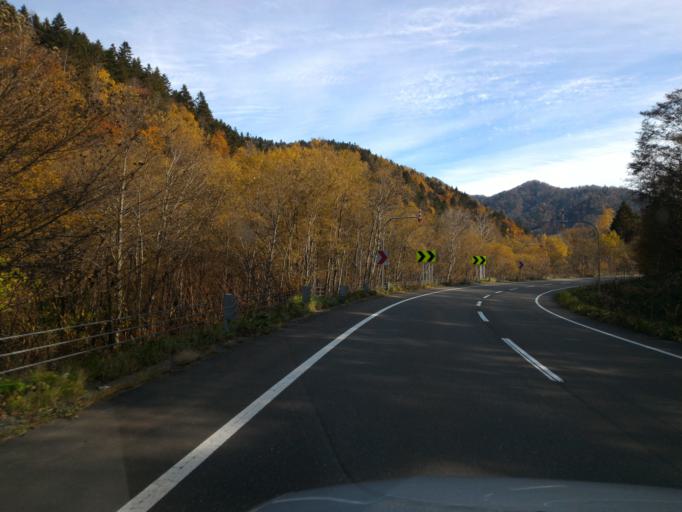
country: JP
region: Hokkaido
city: Ashibetsu
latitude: 43.3687
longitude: 142.2268
